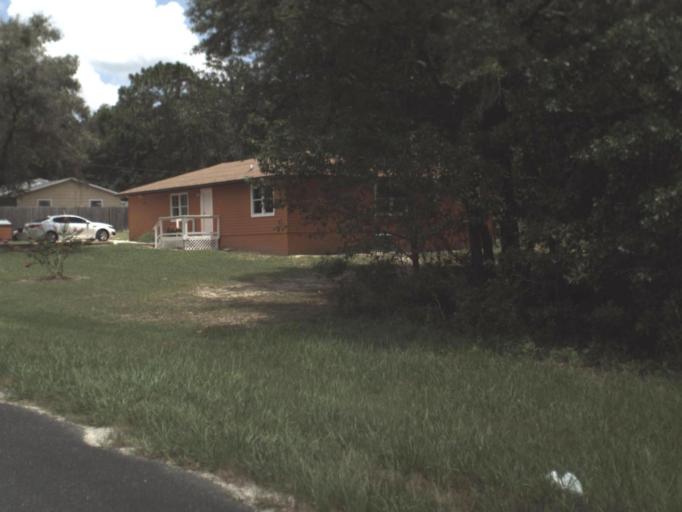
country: US
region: Florida
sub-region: Levy County
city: Williston Highlands
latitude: 29.3370
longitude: -82.5142
